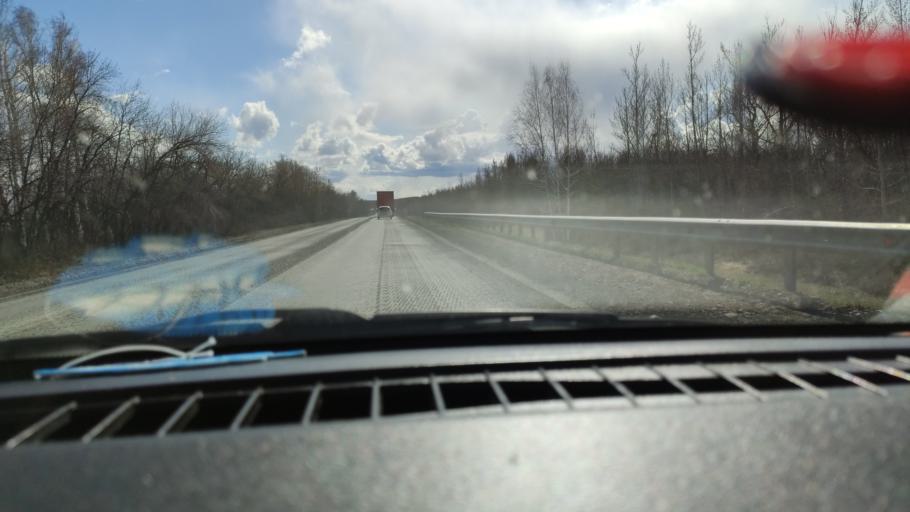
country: RU
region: Saratov
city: Dukhovnitskoye
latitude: 52.6663
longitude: 48.2168
